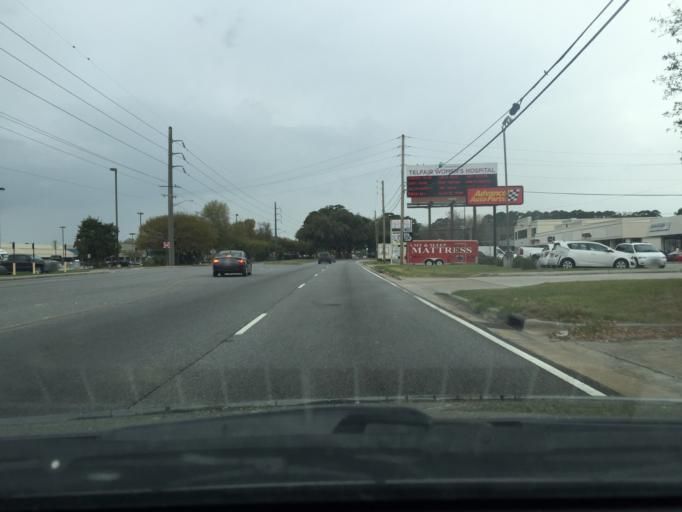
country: US
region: Georgia
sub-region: Chatham County
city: Montgomery
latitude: 31.9985
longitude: -81.1230
